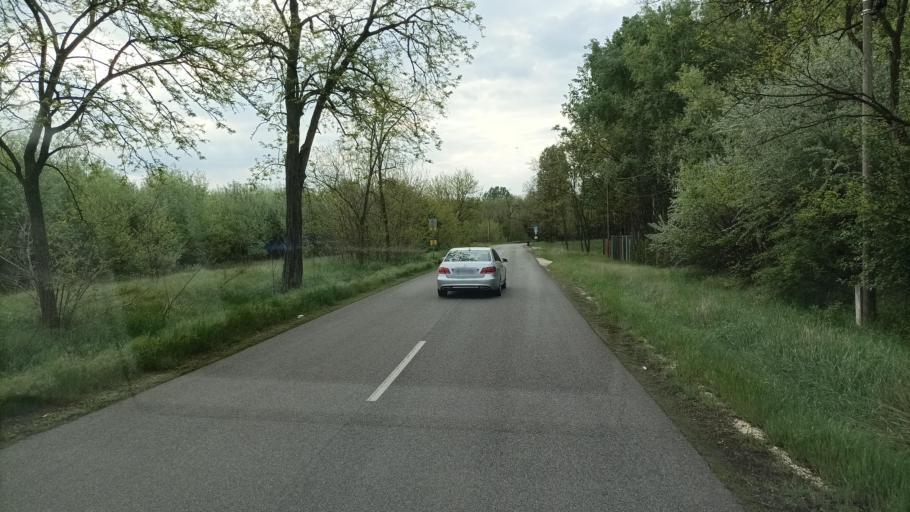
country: HU
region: Pest
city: Monor
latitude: 47.3107
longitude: 19.4200
